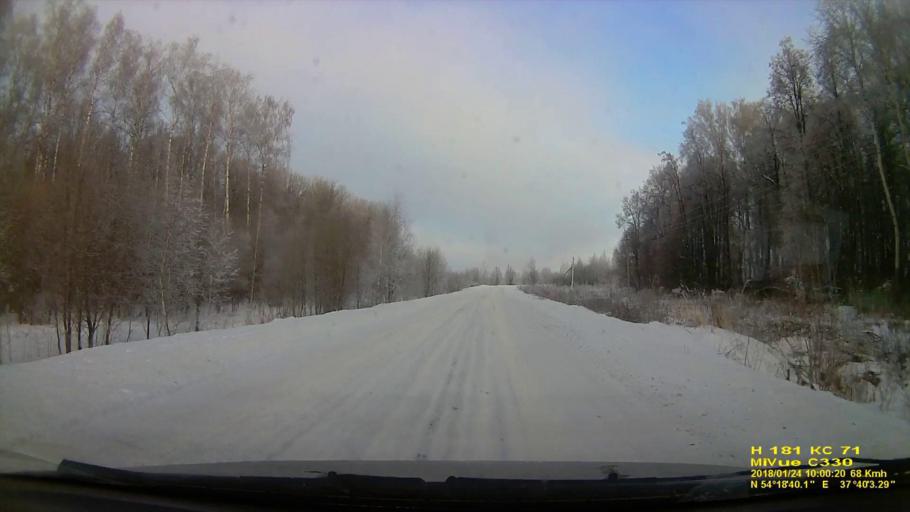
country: RU
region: Tula
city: Revyakino
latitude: 54.3111
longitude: 37.6676
